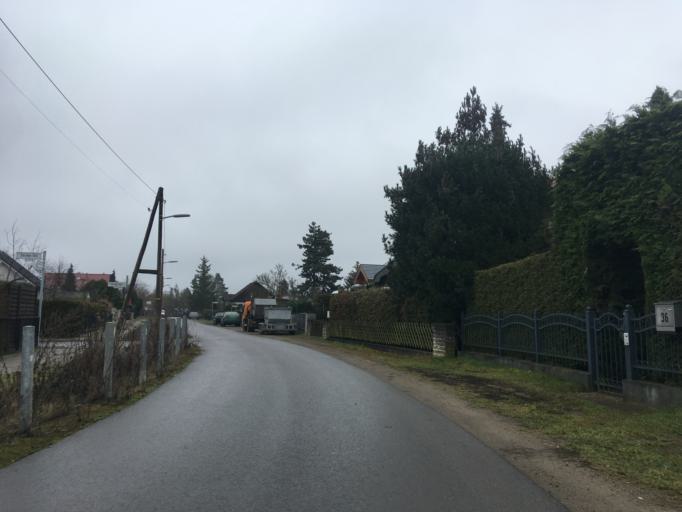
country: DE
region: Berlin
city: Buchholz
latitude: 52.6036
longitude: 13.4399
